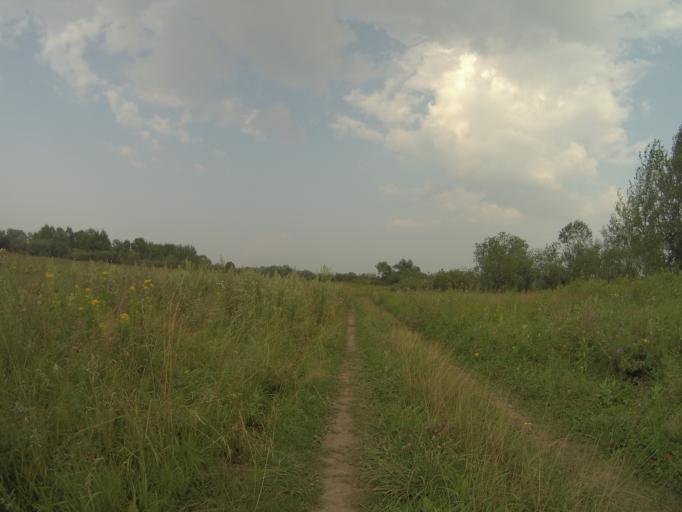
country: RU
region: Vladimir
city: Vladimir
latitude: 56.1031
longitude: 40.3980
